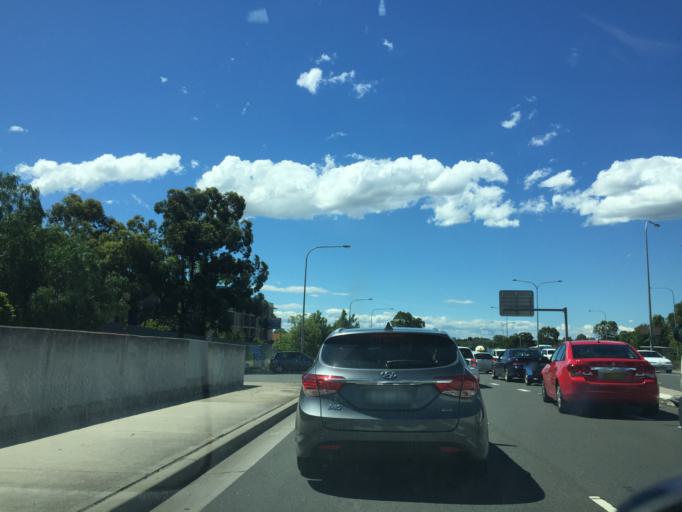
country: AU
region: New South Wales
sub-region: Blacktown
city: Blacktown
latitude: -33.7652
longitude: 150.9128
